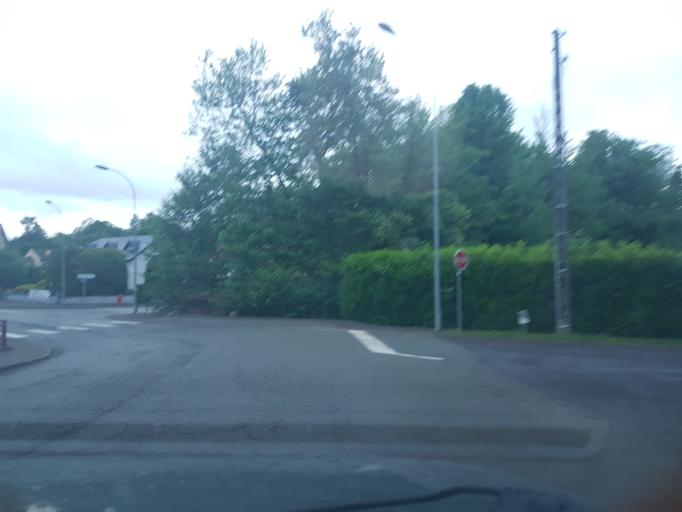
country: FR
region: Franche-Comte
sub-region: Departement de la Haute-Saone
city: Saint-Sauveur
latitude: 47.8198
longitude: 6.3873
